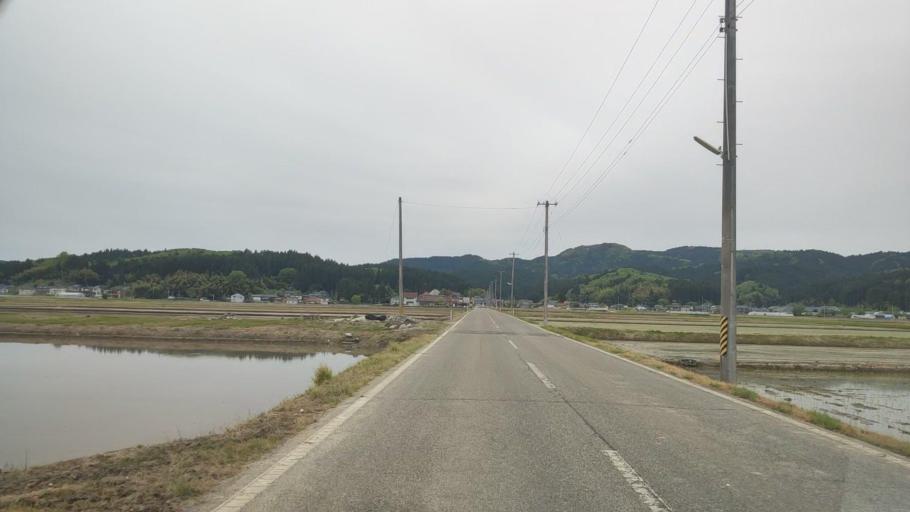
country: JP
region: Niigata
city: Gosen
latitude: 37.7270
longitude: 139.1451
